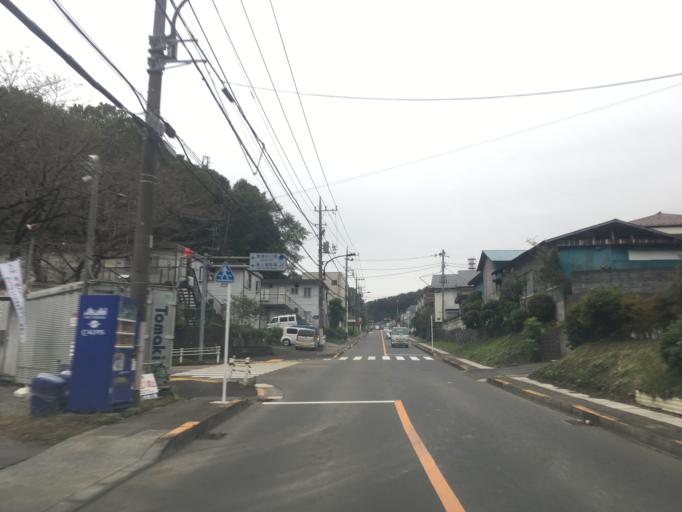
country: JP
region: Tokyo
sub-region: Machida-shi
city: Machida
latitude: 35.5950
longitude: 139.4368
